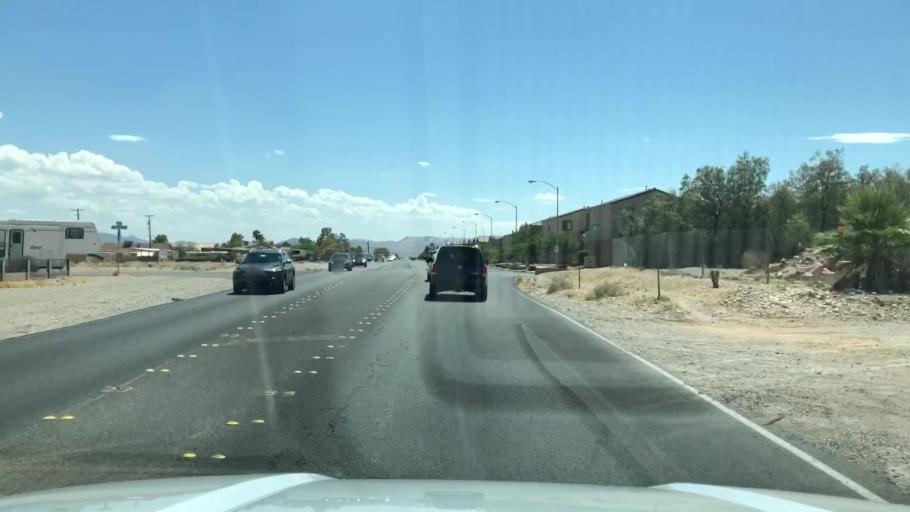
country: US
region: Nevada
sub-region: Clark County
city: Enterprise
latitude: 36.0539
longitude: -115.2079
